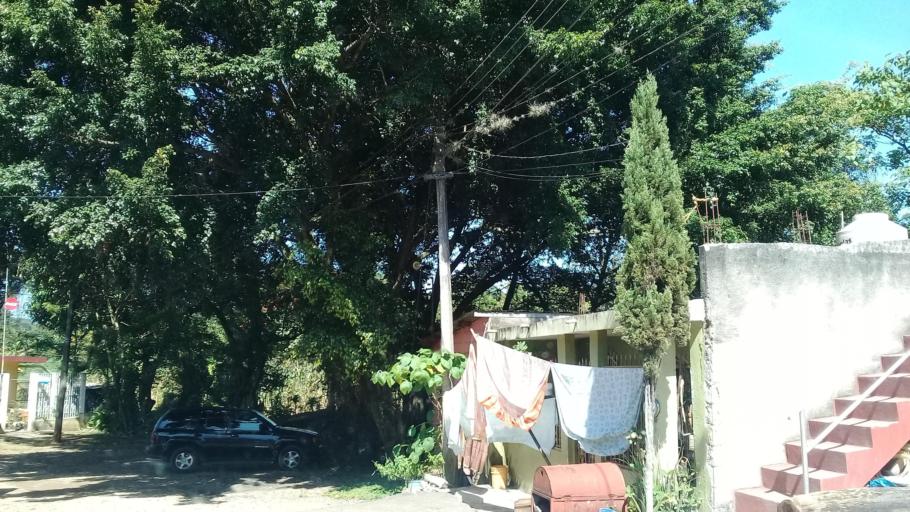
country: MX
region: Veracruz
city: Amatlan de los Reyes
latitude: 18.8530
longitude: -96.9134
